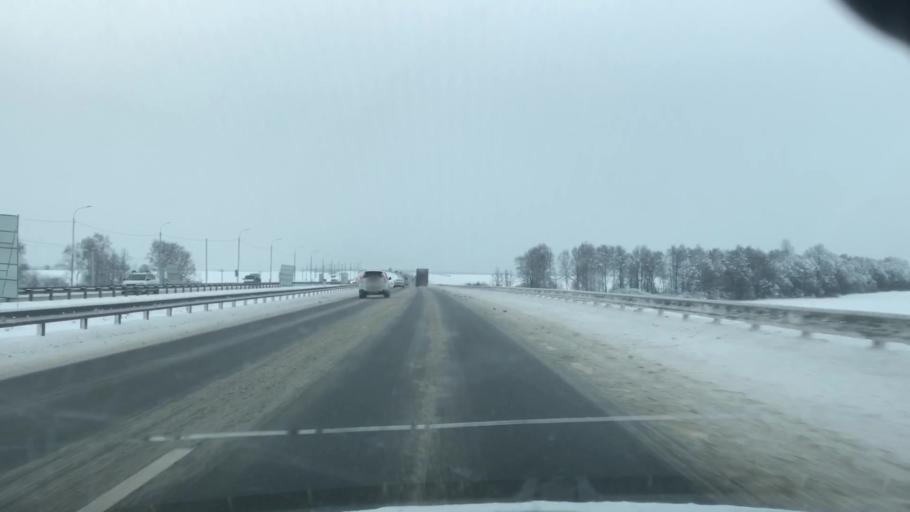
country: RU
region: Moskovskaya
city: Mikhnevo
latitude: 55.1141
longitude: 37.9262
